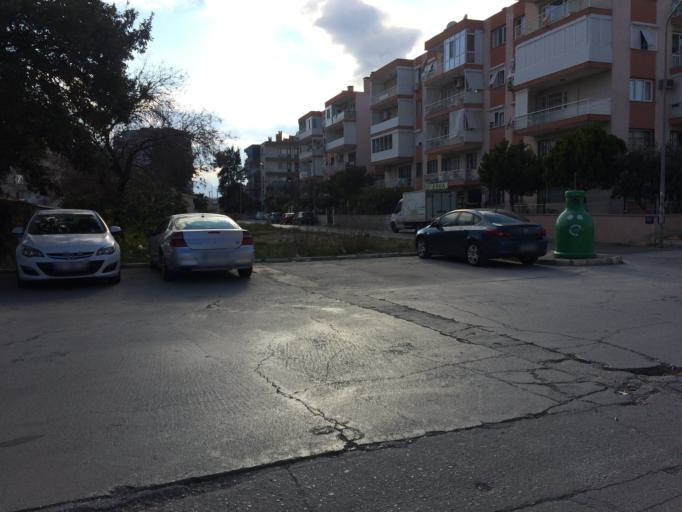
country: TR
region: Izmir
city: Karsiyaka
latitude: 38.4896
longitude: 27.0612
